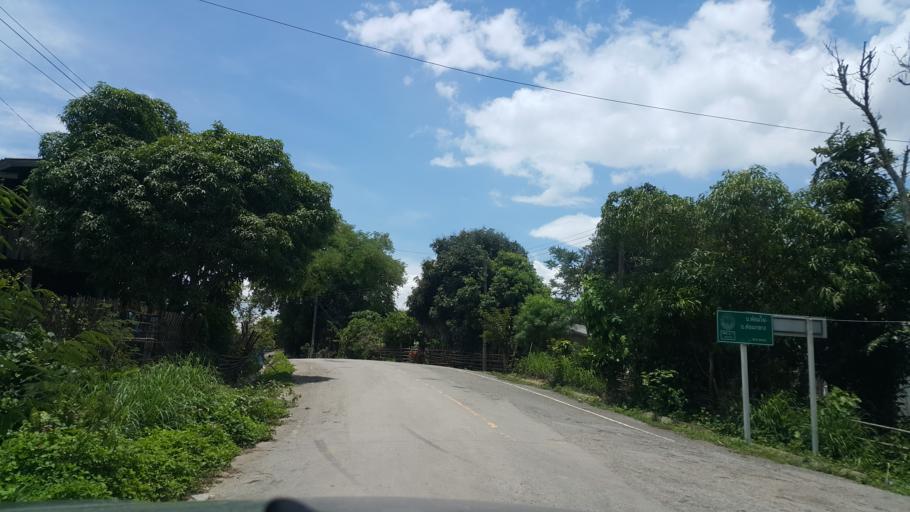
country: TH
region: Phayao
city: Phayao
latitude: 19.1737
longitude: 99.7892
